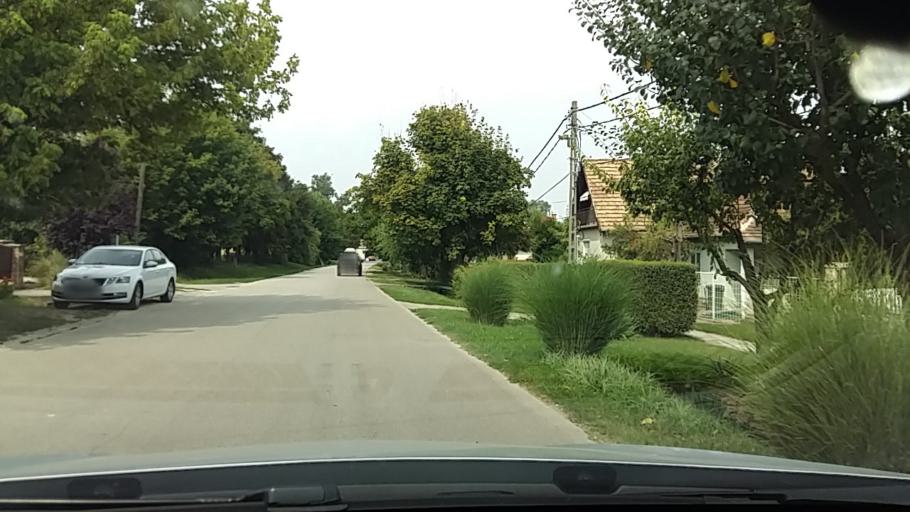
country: HU
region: Fejer
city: Martonvasar
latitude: 47.3206
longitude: 18.7861
